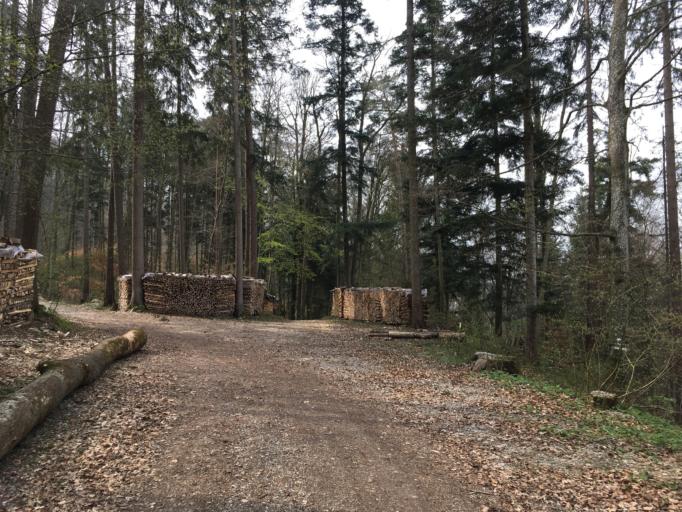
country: DE
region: Bavaria
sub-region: Upper Bavaria
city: Jettenbach
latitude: 48.1643
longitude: 12.3747
